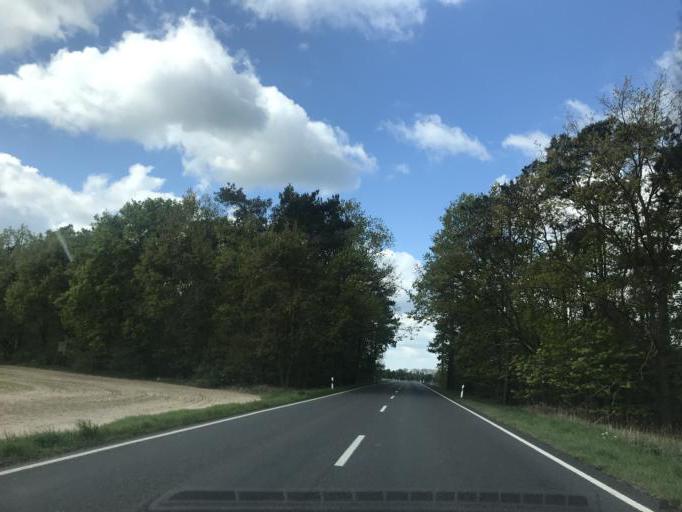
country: DE
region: Brandenburg
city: Liebenwalde
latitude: 52.8763
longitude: 13.4492
